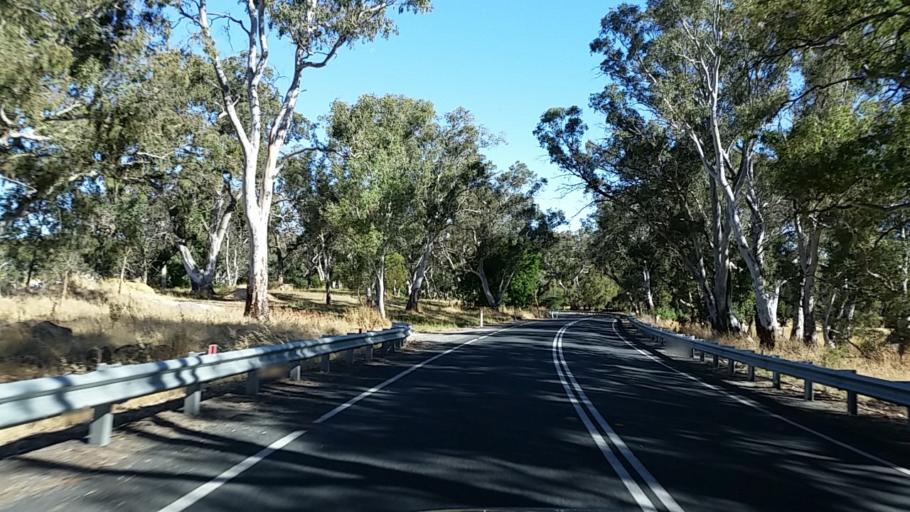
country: AU
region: South Australia
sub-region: Adelaide Hills
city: Birdwood
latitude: -34.7767
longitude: 139.0327
